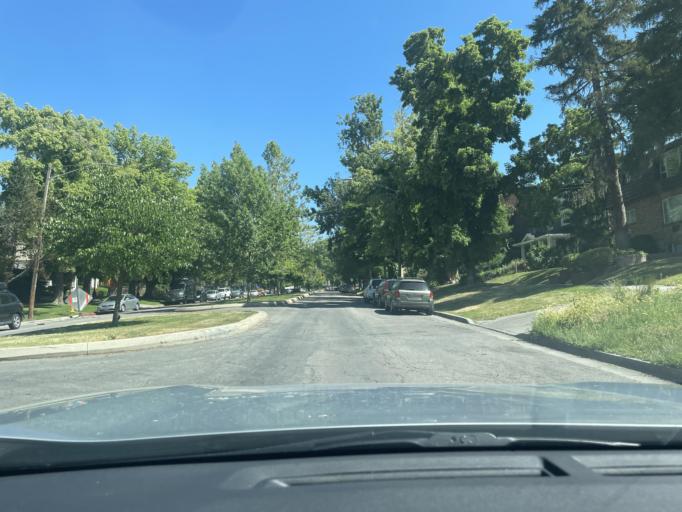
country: US
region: Utah
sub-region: Salt Lake County
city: Salt Lake City
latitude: 40.7657
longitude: -111.8738
